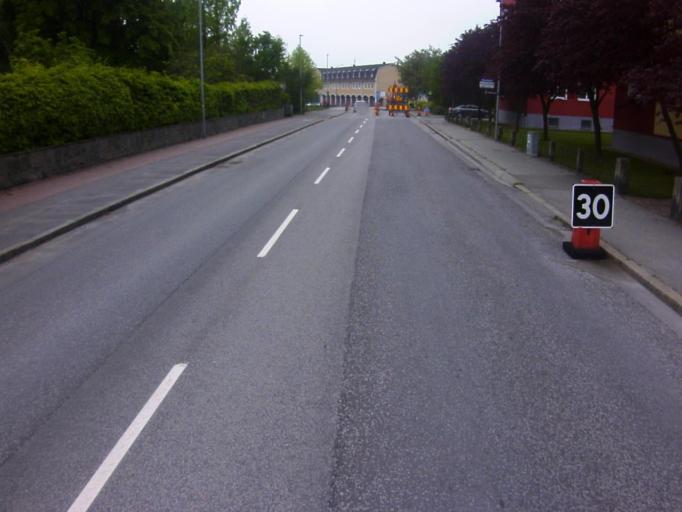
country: SE
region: Blekinge
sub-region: Solvesborgs Kommun
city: Soelvesborg
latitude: 56.0544
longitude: 14.5851
